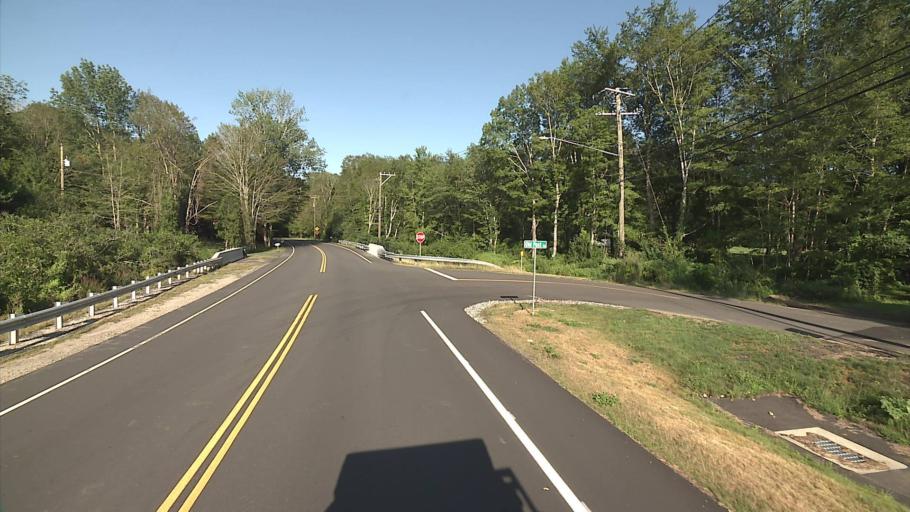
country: US
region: Connecticut
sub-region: Middlesex County
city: Old Saybrook Center
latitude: 41.3507
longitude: -72.2902
